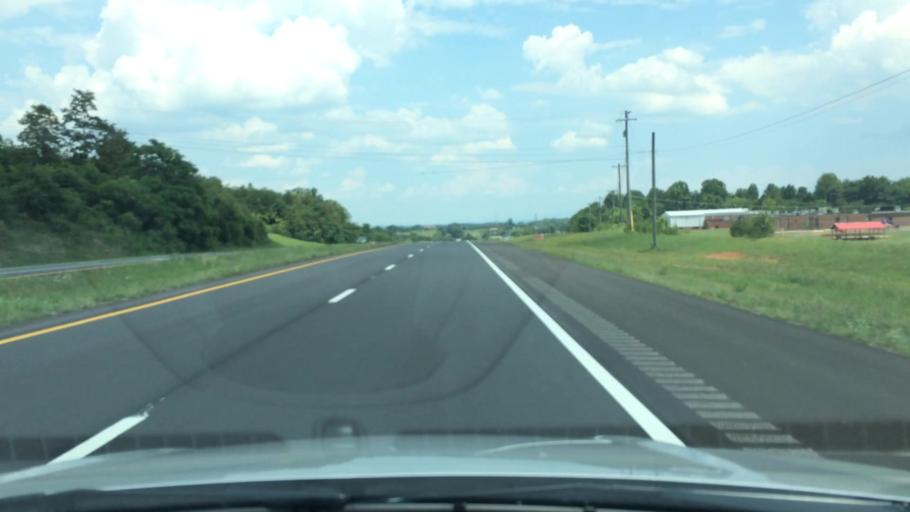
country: US
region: Tennessee
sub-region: Hamblen County
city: Morristown
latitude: 36.1828
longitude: -83.2471
